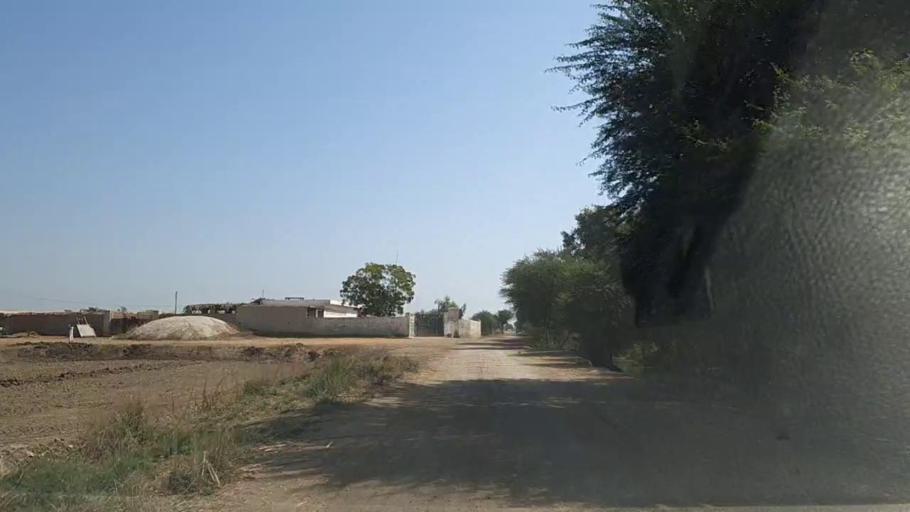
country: PK
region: Sindh
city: Samaro
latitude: 25.2715
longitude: 69.4050
